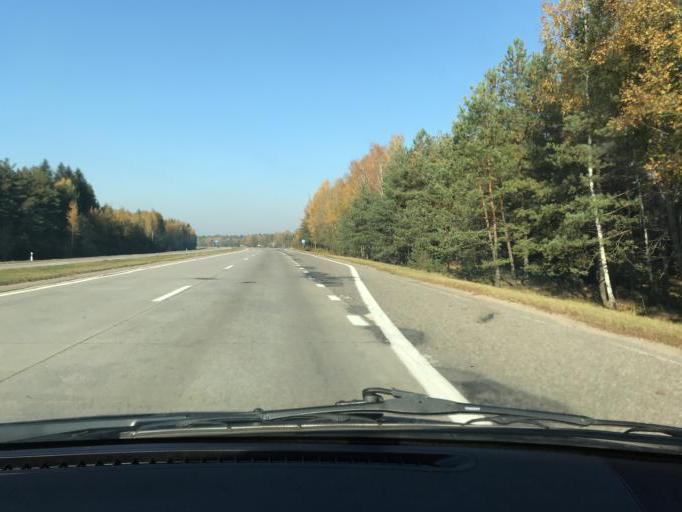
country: BY
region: Minsk
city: Uzda
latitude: 53.3664
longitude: 27.5084
